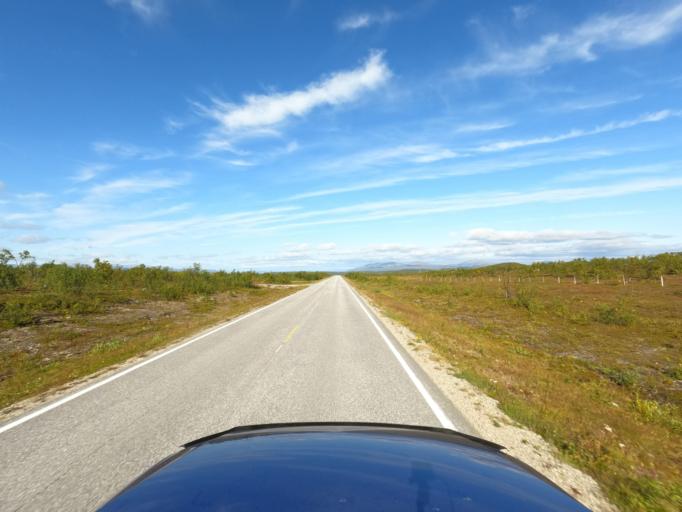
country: NO
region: Finnmark Fylke
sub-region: Karasjok
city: Karasjohka
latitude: 69.7181
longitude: 25.2386
